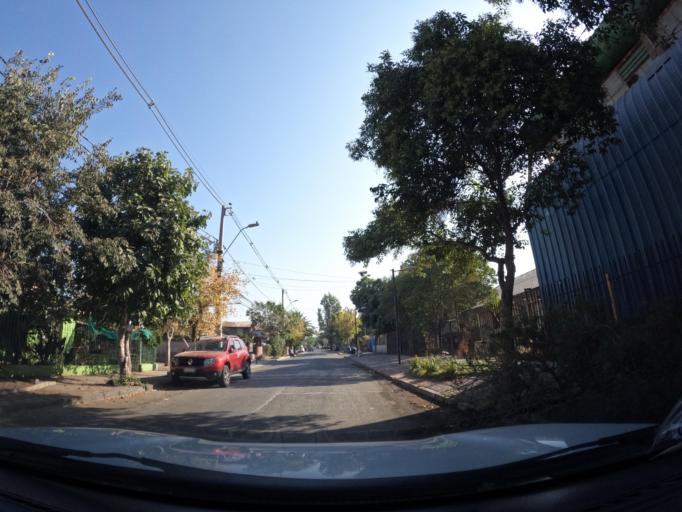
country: CL
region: Santiago Metropolitan
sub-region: Provincia de Santiago
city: Villa Presidente Frei, Nunoa, Santiago, Chile
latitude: -33.5087
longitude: -70.5692
